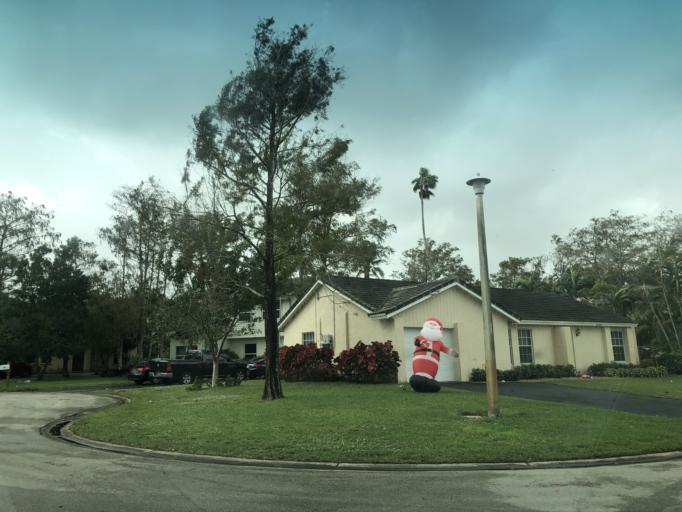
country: US
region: Florida
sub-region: Broward County
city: Tamarac
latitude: 26.2459
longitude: -80.2466
